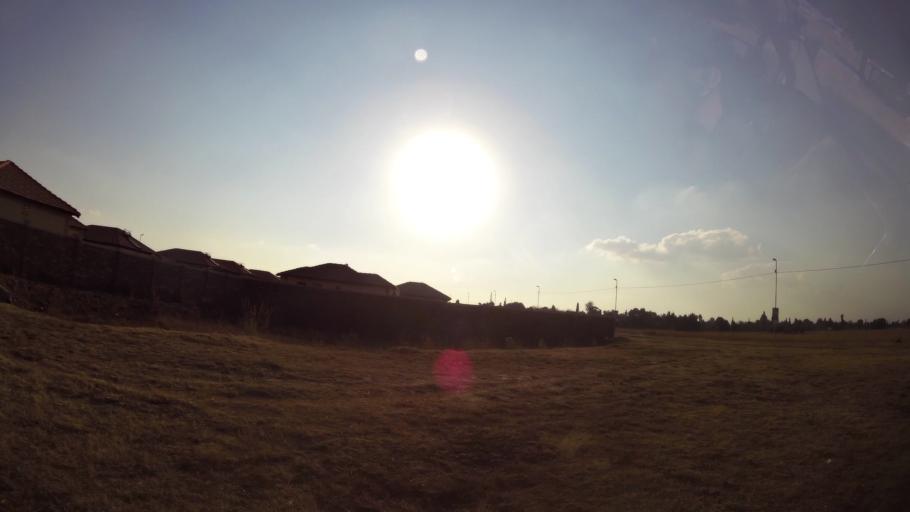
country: ZA
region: Gauteng
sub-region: Ekurhuleni Metropolitan Municipality
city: Benoni
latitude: -26.1406
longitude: 28.3761
